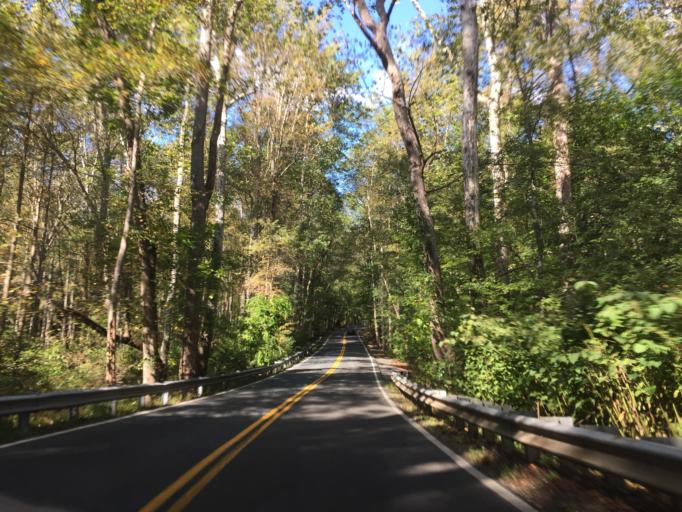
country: US
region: Maryland
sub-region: Harford County
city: Fallston
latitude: 39.5072
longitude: -76.4593
